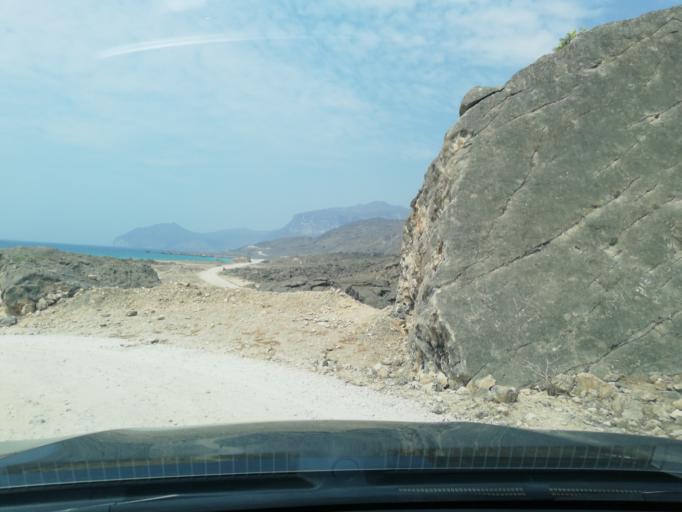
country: OM
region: Zufar
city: Salalah
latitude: 16.8297
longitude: 53.7070
